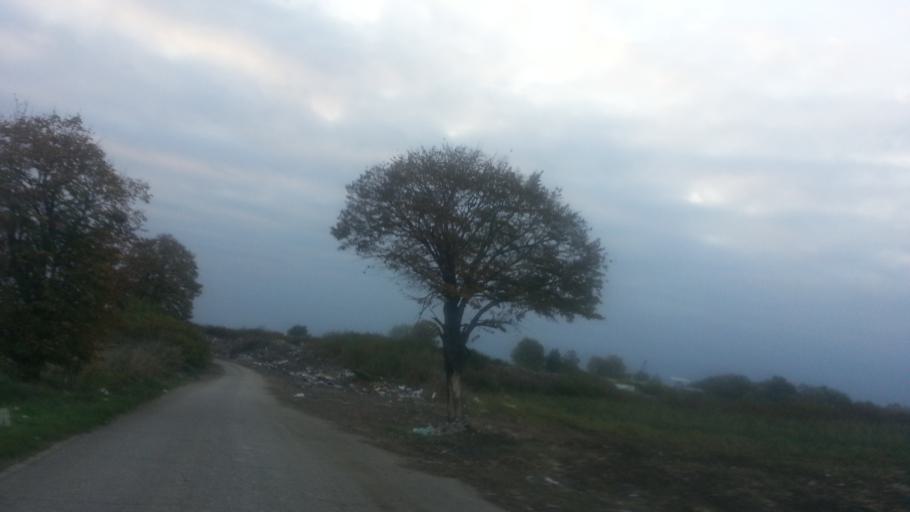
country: RS
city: Novi Banovci
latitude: 44.9174
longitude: 20.3085
